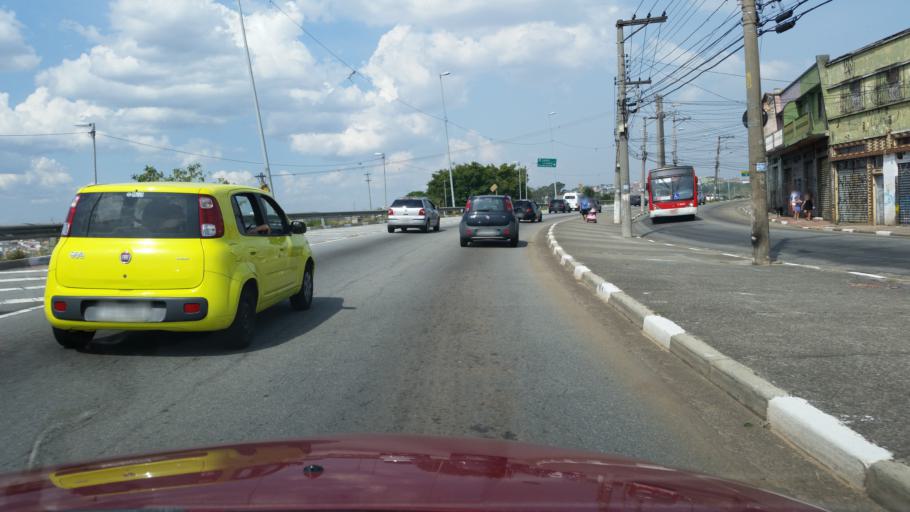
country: BR
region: Sao Paulo
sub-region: Ferraz De Vasconcelos
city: Ferraz de Vasconcelos
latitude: -23.5251
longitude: -46.4349
